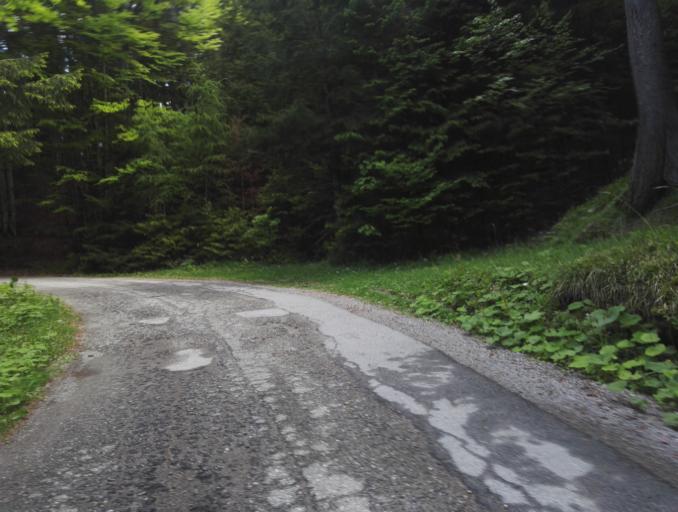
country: AT
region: Styria
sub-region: Politischer Bezirk Graz-Umgebung
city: Sankt Radegund bei Graz
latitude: 47.2024
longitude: 15.4511
